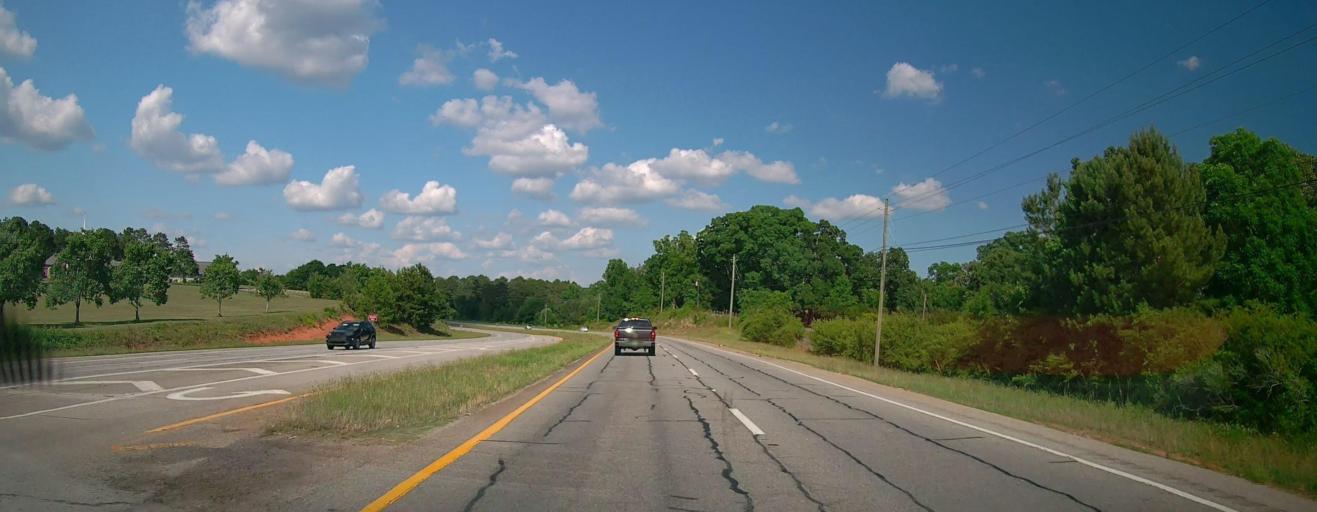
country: US
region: Georgia
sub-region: Henry County
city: Hampton
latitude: 33.3957
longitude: -84.2464
